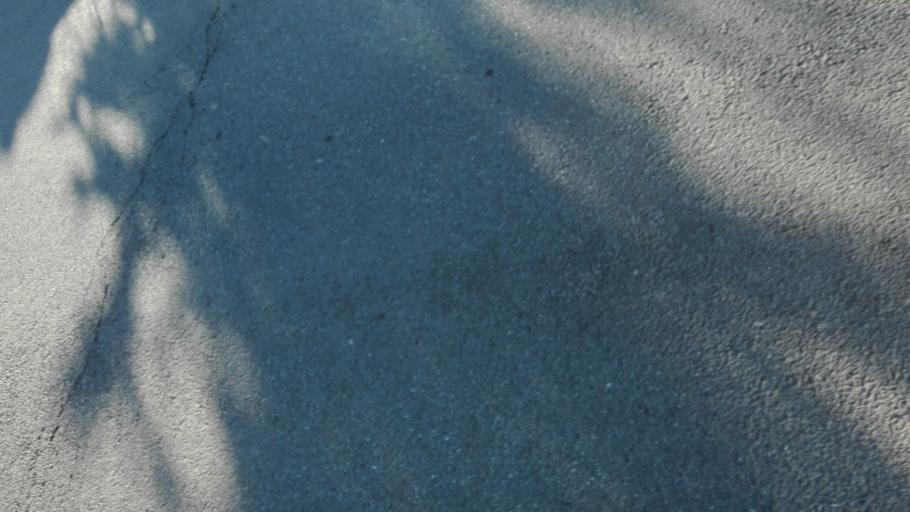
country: FR
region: Midi-Pyrenees
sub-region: Departement de la Haute-Garonne
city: Grenade
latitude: 43.7568
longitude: 1.2989
